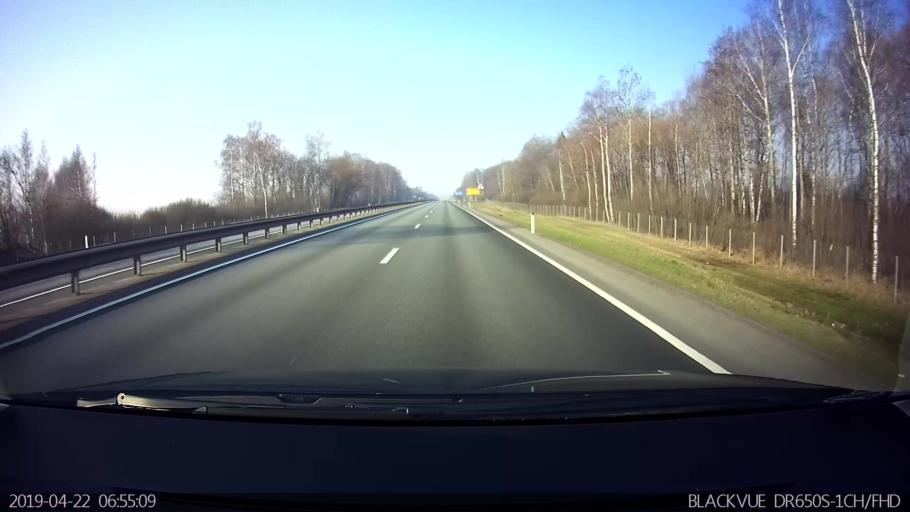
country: RU
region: Smolensk
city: Gagarin
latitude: 55.4626
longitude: 34.8911
